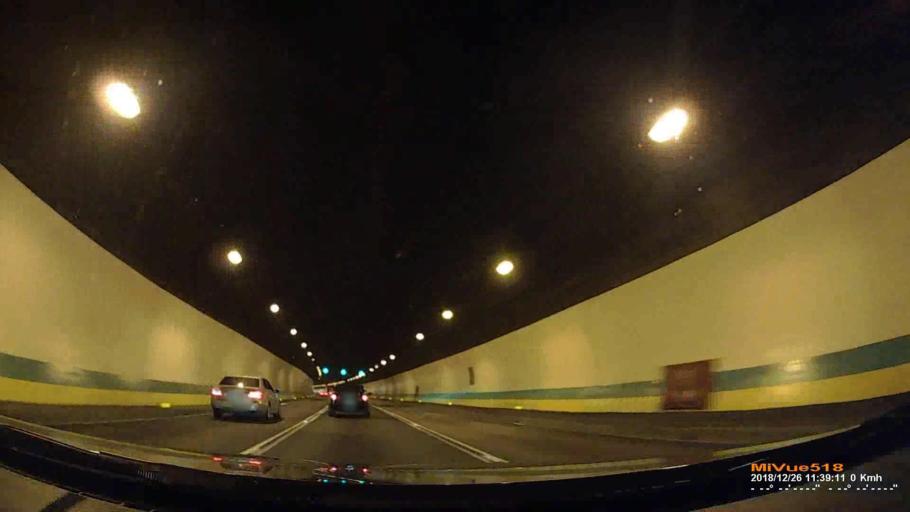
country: TW
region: Taipei
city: Taipei
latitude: 24.9882
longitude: 121.5902
